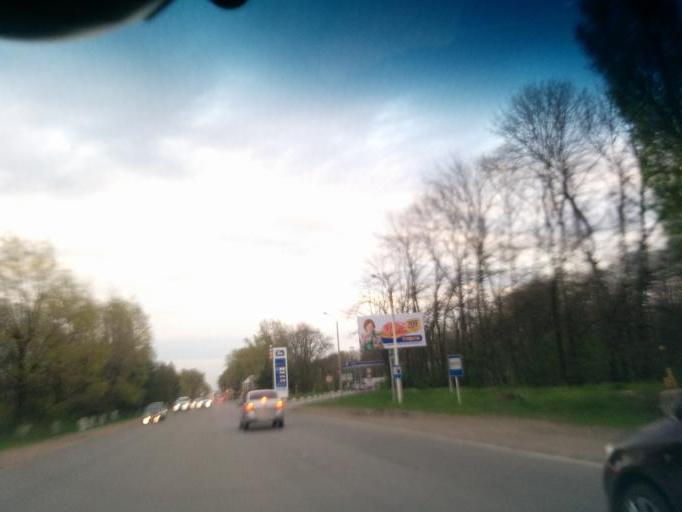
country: RU
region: Rostov
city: Novocherkassk
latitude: 47.4197
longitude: 40.0280
